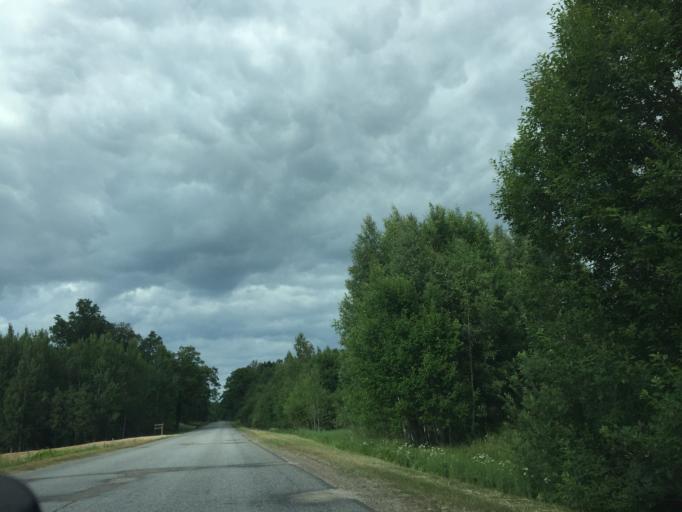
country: LV
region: Skriveri
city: Skriveri
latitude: 56.8275
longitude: 25.1256
